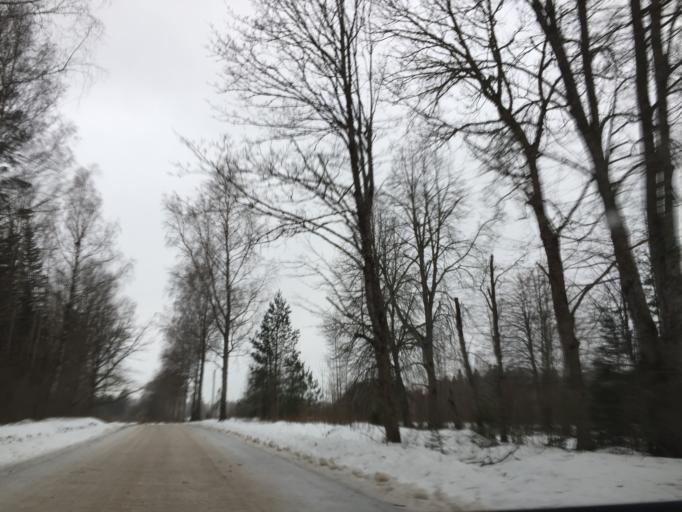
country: LV
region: Salacgrivas
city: Salacgriva
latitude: 57.6495
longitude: 24.4787
